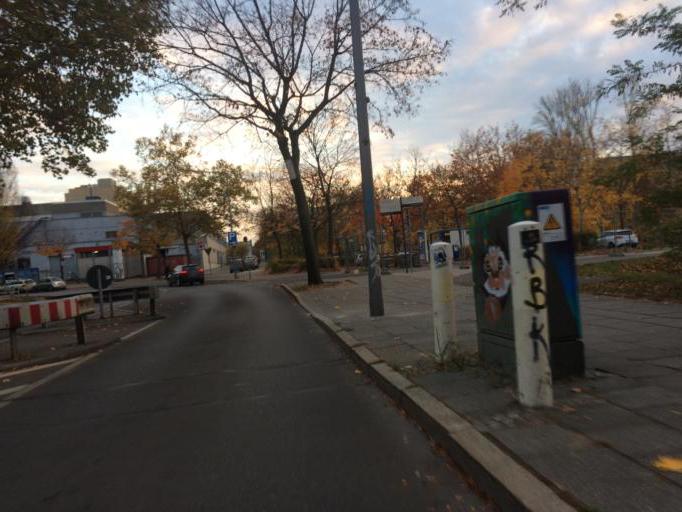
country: DE
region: Berlin
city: Markisches Viertel
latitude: 52.6004
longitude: 13.3532
